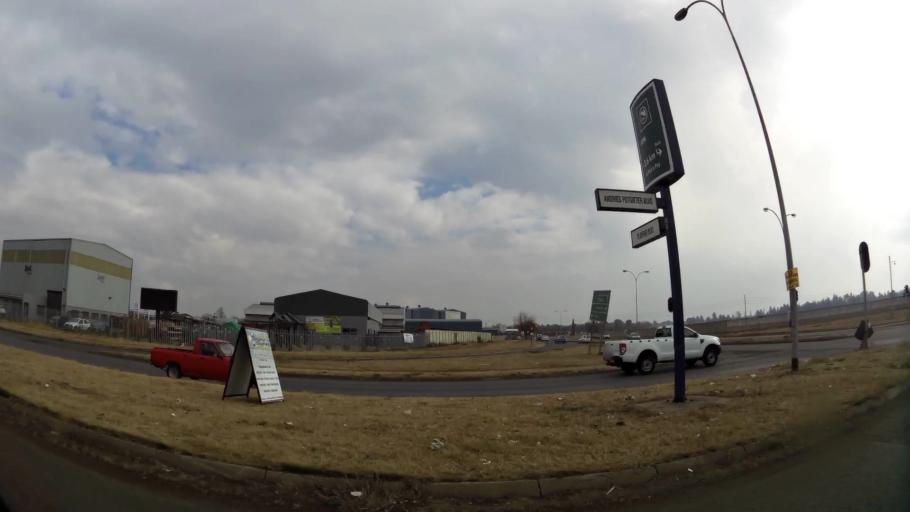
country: ZA
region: Gauteng
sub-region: Sedibeng District Municipality
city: Vanderbijlpark
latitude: -26.7017
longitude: 27.8600
